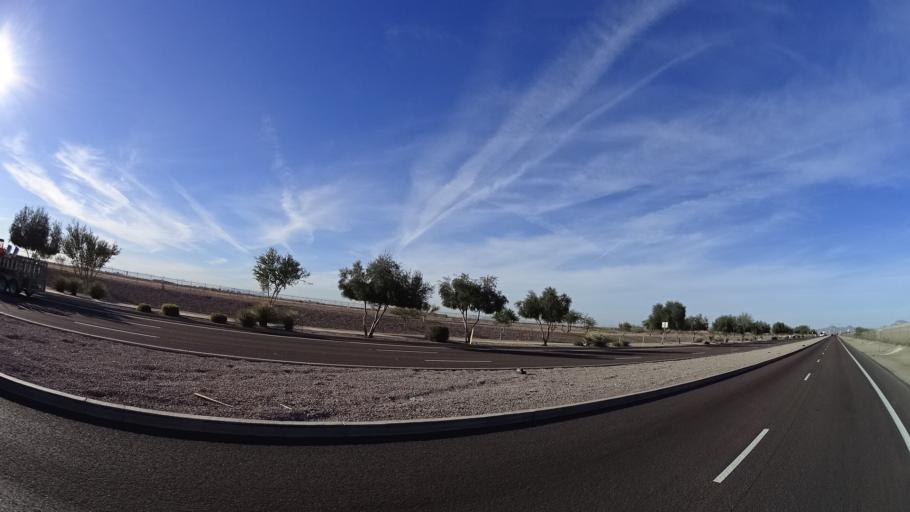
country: US
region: Arizona
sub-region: Maricopa County
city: Queen Creek
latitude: 33.3093
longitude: -111.6353
